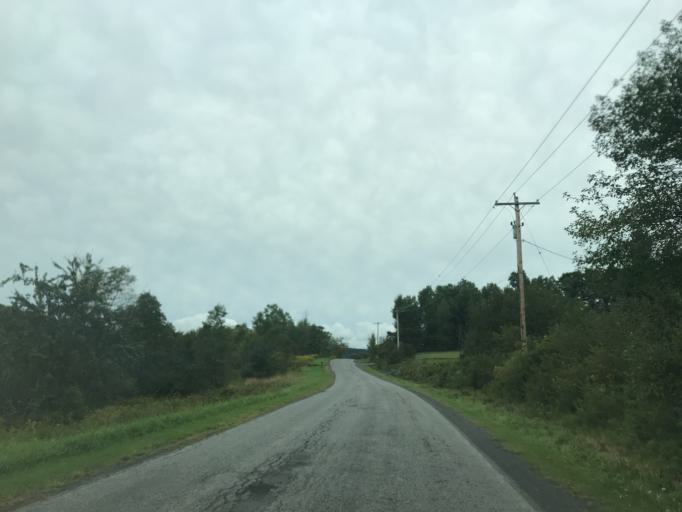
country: US
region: New York
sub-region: Otsego County
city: Worcester
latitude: 42.5625
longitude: -74.6687
